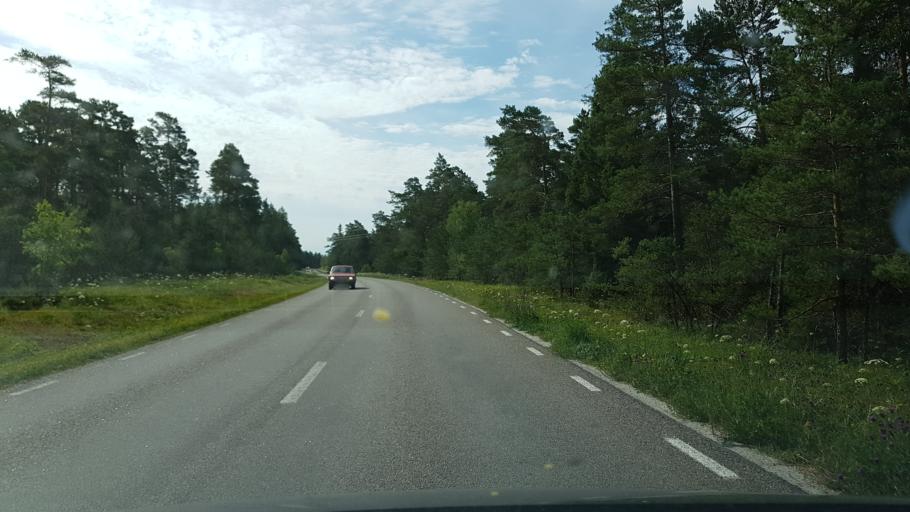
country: SE
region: Gotland
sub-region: Gotland
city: Hemse
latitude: 57.4612
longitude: 18.5729
